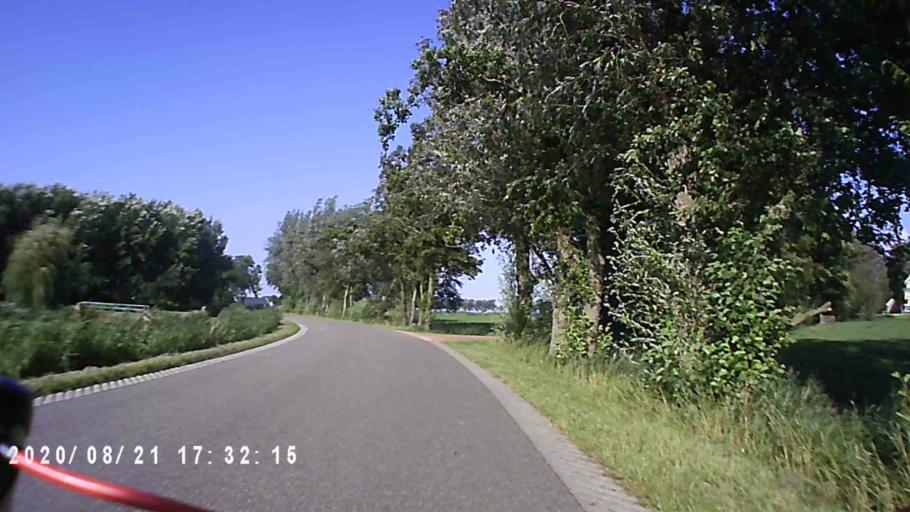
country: NL
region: Groningen
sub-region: Gemeente Bedum
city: Bedum
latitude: 53.2762
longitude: 6.5906
